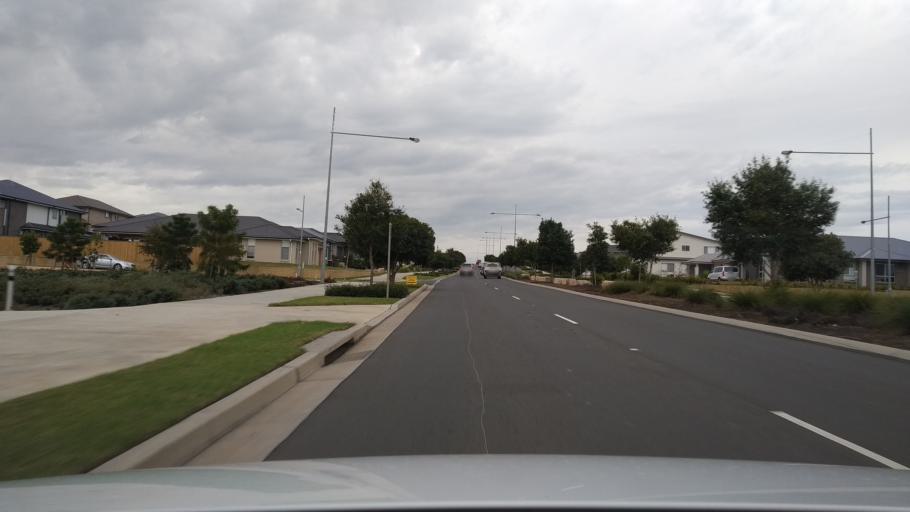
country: AU
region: New South Wales
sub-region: Camden
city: Narellan
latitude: -34.0059
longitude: 150.7253
